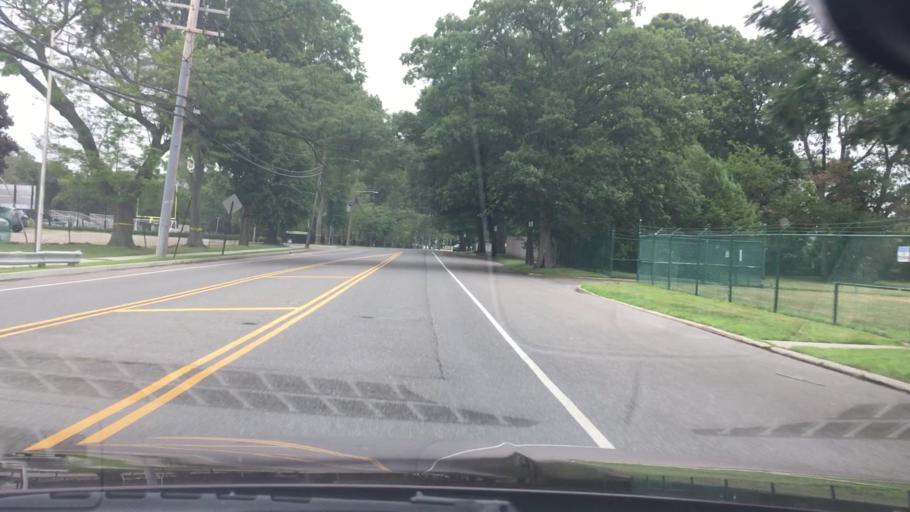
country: US
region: New York
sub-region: Suffolk County
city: South Huntington
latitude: 40.8113
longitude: -73.3905
